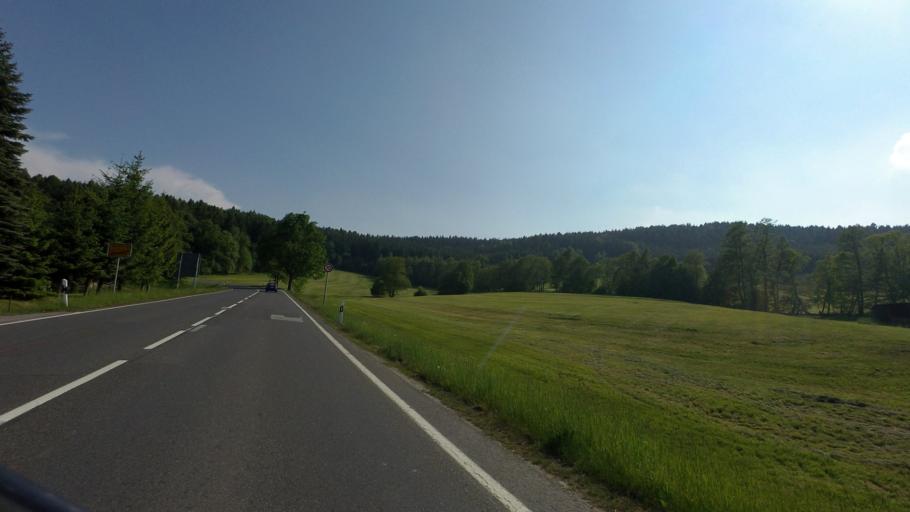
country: DE
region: Saxony
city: Oppach
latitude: 51.0807
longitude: 14.4846
